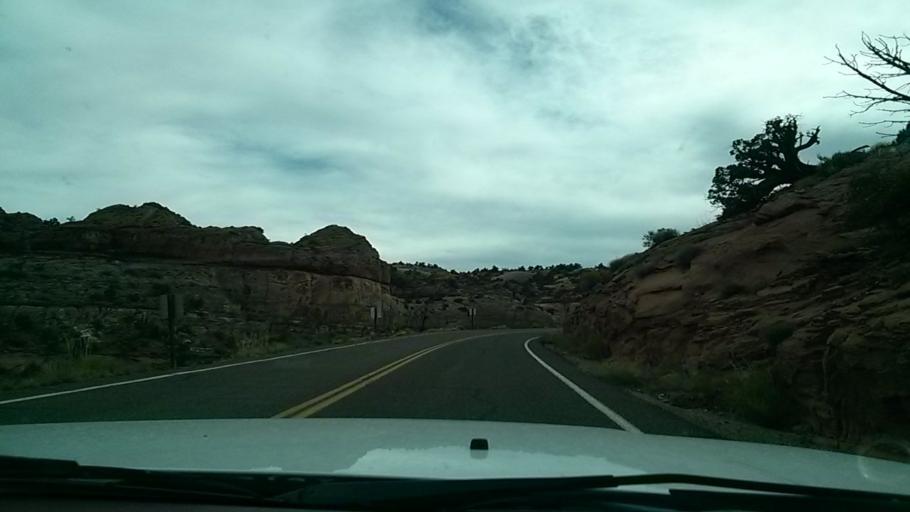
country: US
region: Utah
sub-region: Wayne County
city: Loa
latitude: 37.7721
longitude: -111.4160
